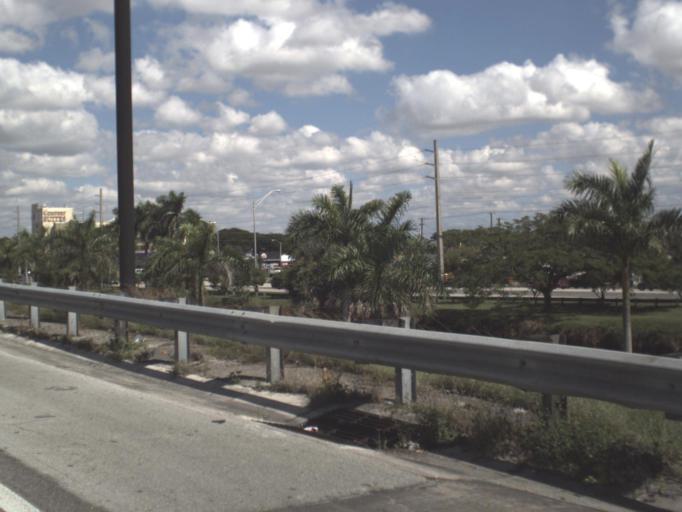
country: US
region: Florida
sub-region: Miami-Dade County
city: Westwood Lake
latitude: 25.7301
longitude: -80.3840
